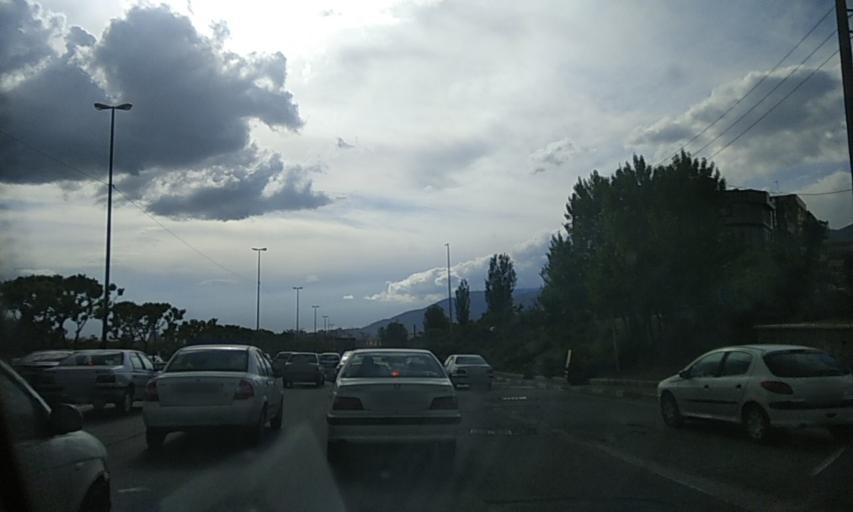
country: IR
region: Tehran
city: Tehran
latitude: 35.7538
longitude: 51.2852
